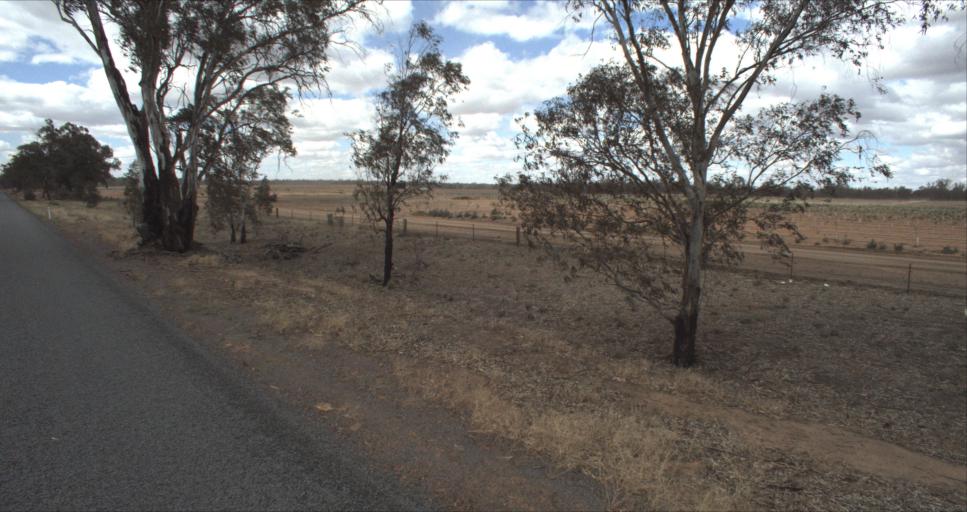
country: AU
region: New South Wales
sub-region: Leeton
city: Leeton
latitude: -34.6543
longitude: 146.3506
